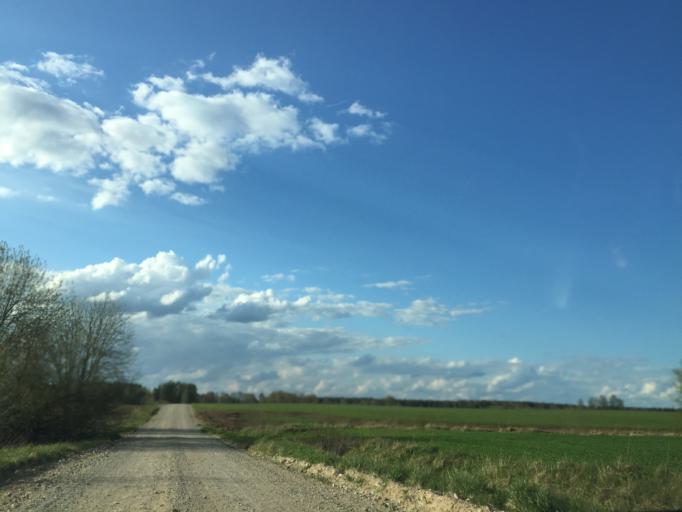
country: LV
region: Beverina
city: Murmuiza
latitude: 57.3872
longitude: 25.4836
